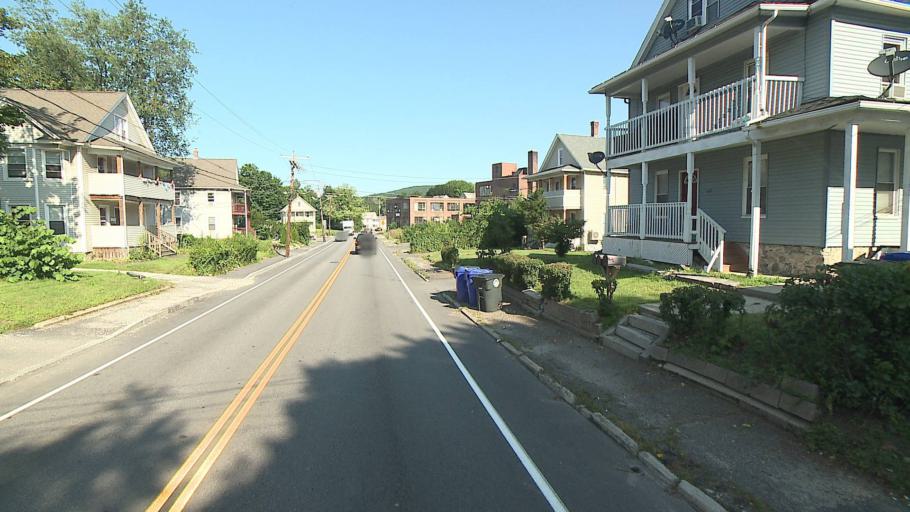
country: US
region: Connecticut
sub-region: Litchfield County
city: Torrington
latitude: 41.8081
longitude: -73.1155
